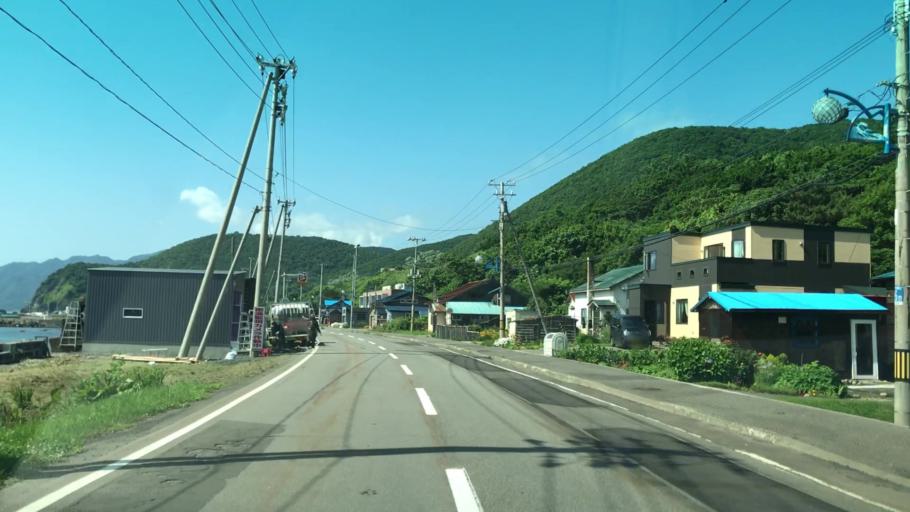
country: JP
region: Hokkaido
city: Iwanai
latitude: 43.0945
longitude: 140.4634
